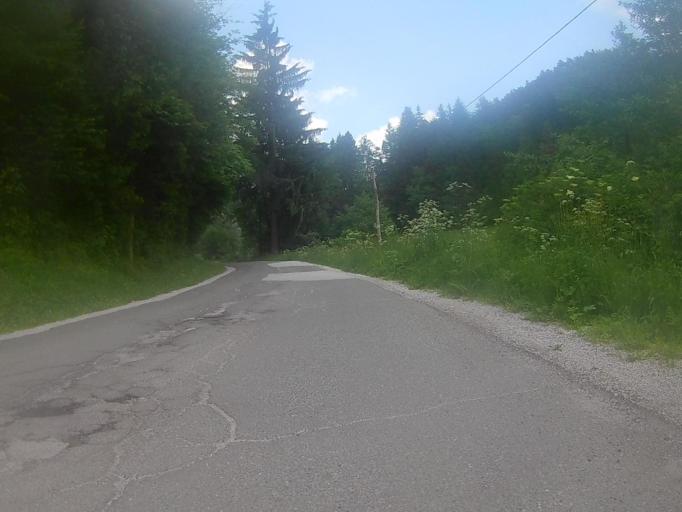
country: SI
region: Maribor
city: Bresternica
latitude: 46.6182
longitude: 15.5545
